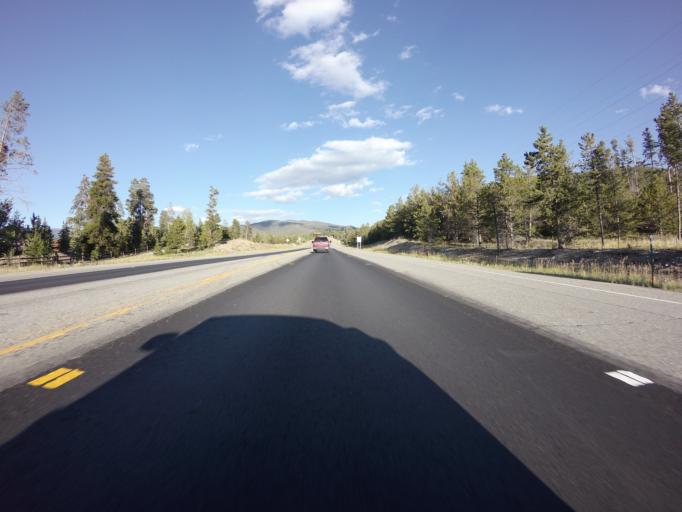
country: US
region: Colorado
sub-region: Summit County
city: Frisco
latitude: 39.5732
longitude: -106.0832
